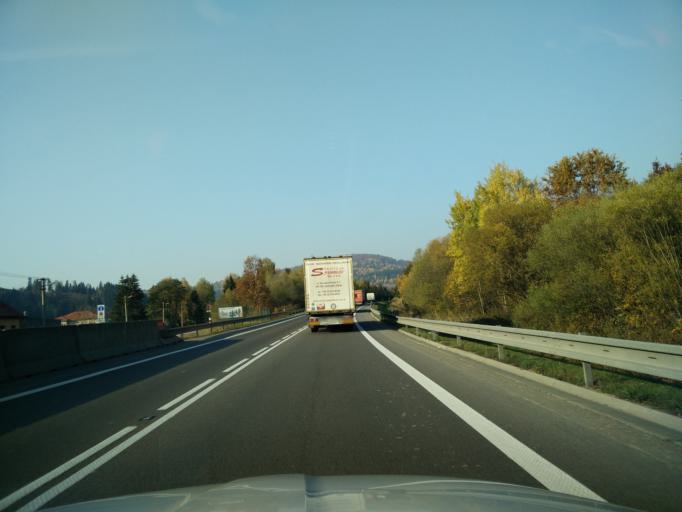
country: SK
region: Zilinsky
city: Cadca
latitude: 49.4146
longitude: 18.8386
